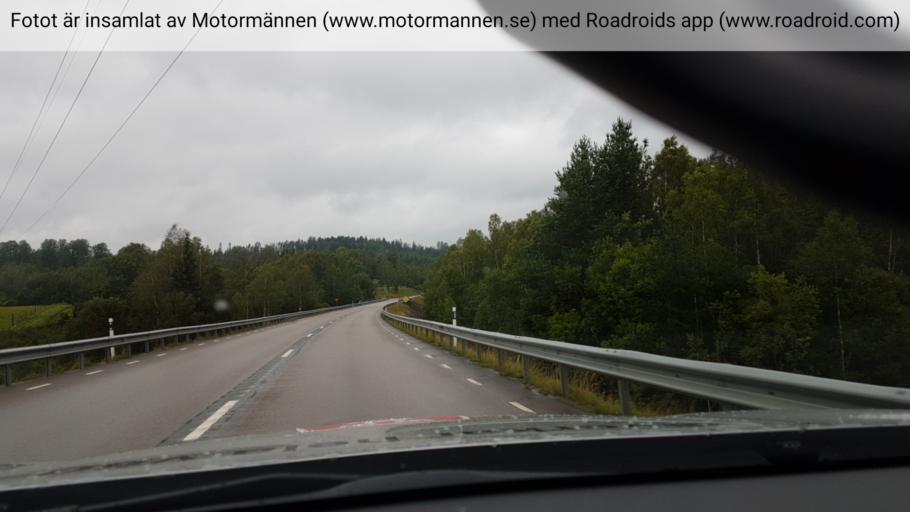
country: SE
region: Vaestra Goetaland
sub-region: Bengtsfors Kommun
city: Billingsfors
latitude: 58.9285
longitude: 12.1380
